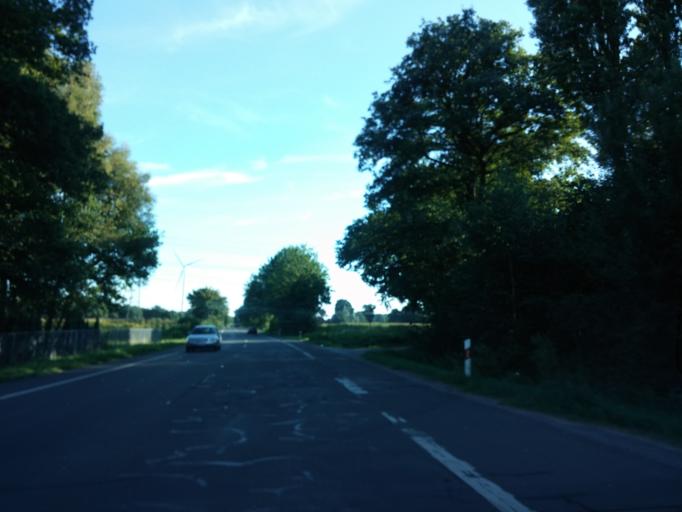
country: DE
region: North Rhine-Westphalia
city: Dorsten
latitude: 51.6357
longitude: 6.9588
